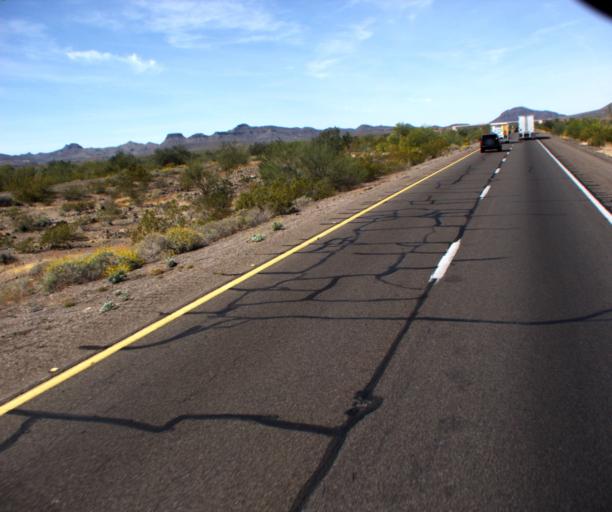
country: US
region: Arizona
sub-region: La Paz County
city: Quartzsite
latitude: 33.6556
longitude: -113.9570
